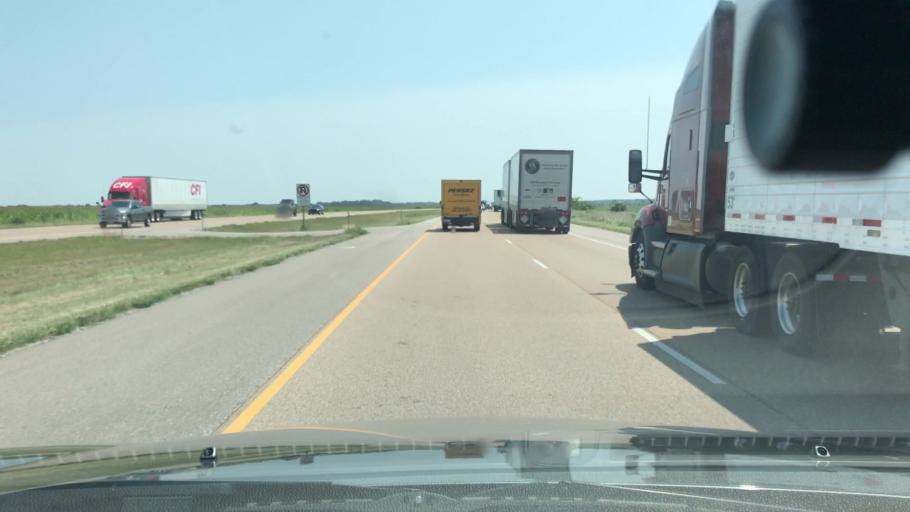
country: US
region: Illinois
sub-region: Washington County
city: Okawville
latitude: 38.4273
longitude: -89.4692
